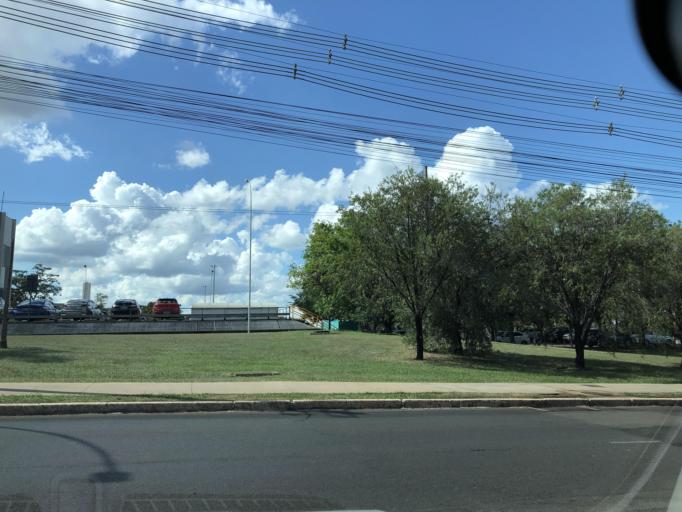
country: BR
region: Federal District
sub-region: Brasilia
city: Brasilia
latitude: -15.7827
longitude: -47.9077
